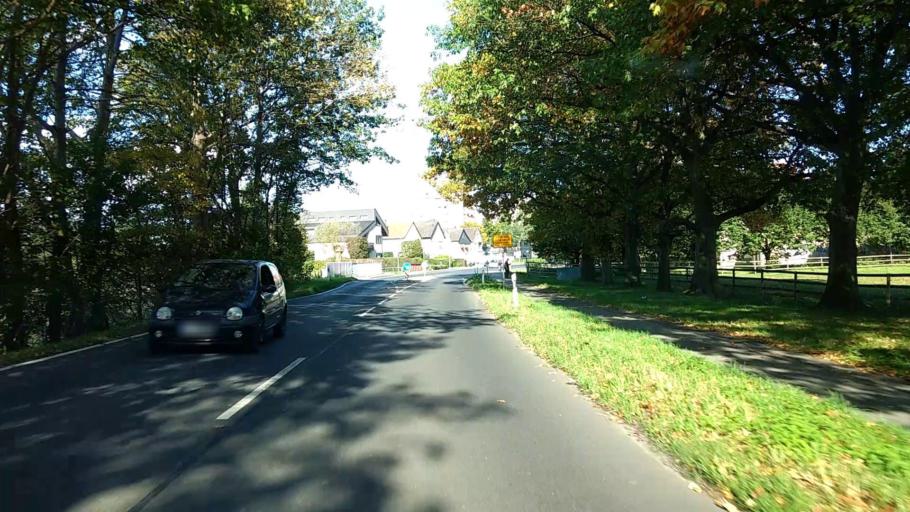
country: DE
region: North Rhine-Westphalia
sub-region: Regierungsbezirk Koln
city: Bergheim
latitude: 50.9285
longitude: 6.6844
